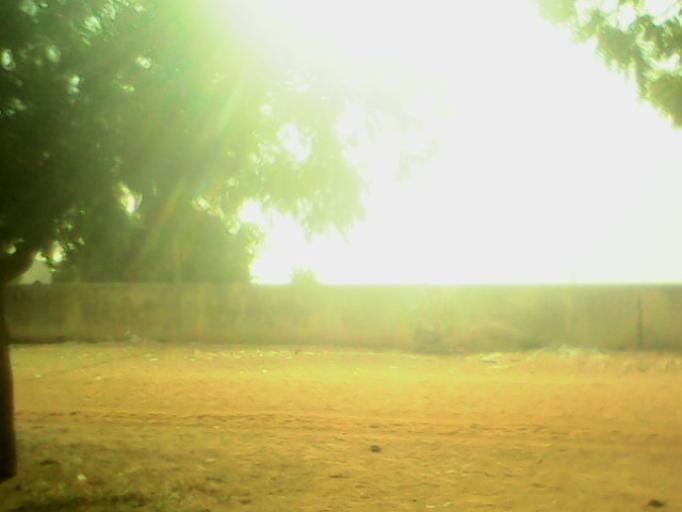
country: SN
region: Diourbel
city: Touba
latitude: 14.8621
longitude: -15.8960
